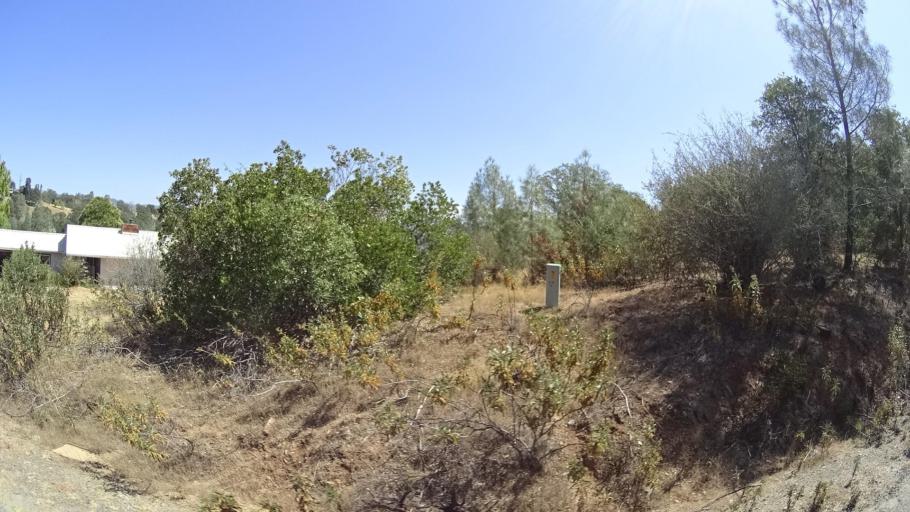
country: US
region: California
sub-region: Mariposa County
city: Mariposa
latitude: 37.4535
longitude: -119.9089
